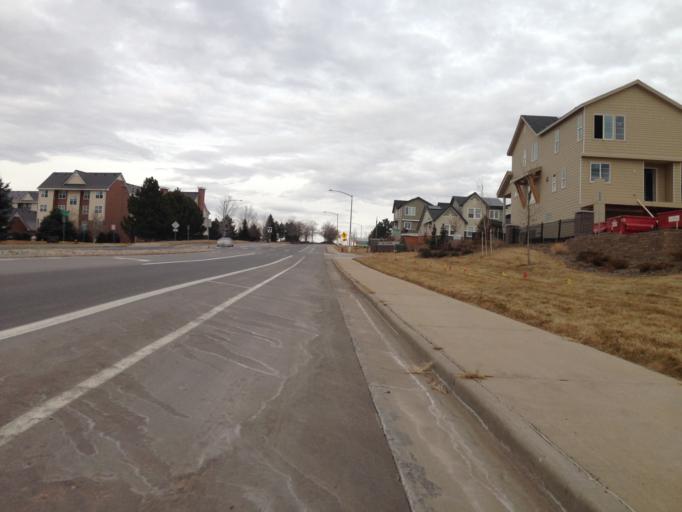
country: US
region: Colorado
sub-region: Adams County
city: Westminster
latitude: 39.8575
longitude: -105.0514
